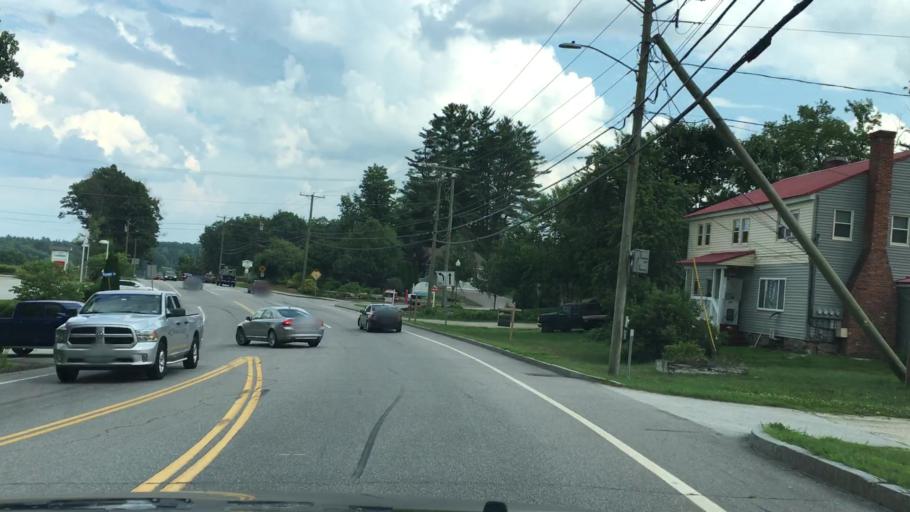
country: US
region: New Hampshire
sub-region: Belknap County
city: Meredith
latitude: 43.6060
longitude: -71.4651
